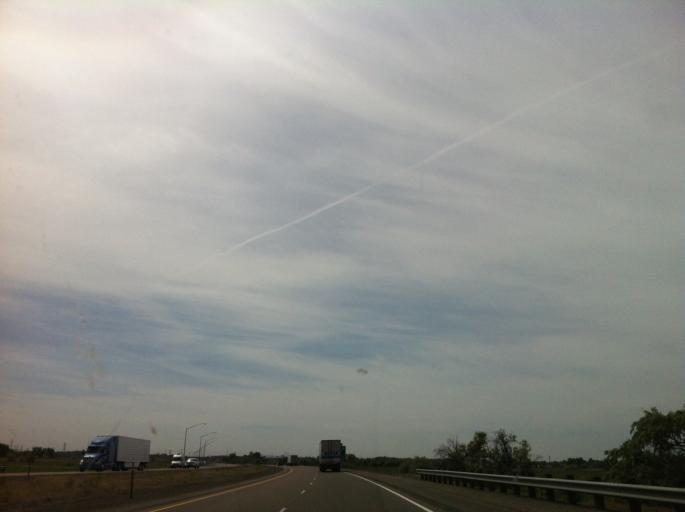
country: US
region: Oregon
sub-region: Malheur County
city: Ontario
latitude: 44.0656
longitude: -116.9954
